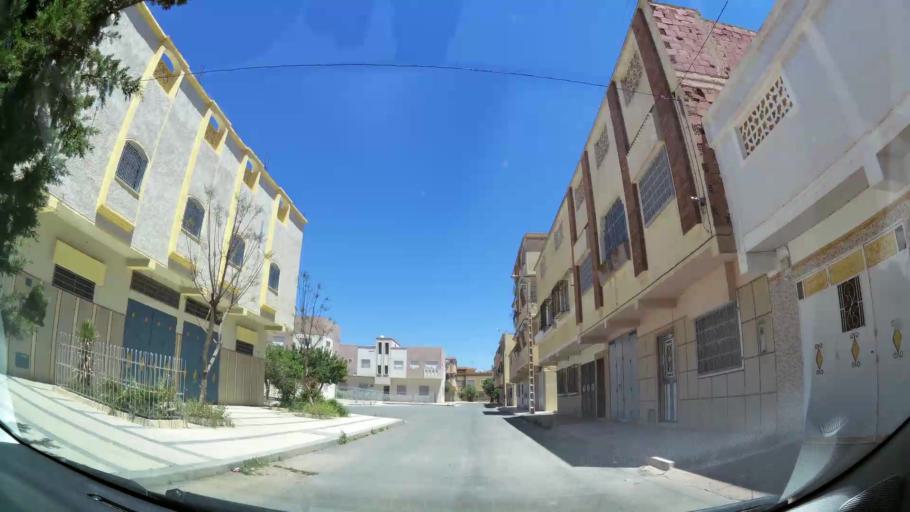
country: MA
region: Oriental
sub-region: Oujda-Angad
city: Oujda
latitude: 34.6774
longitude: -1.8771
